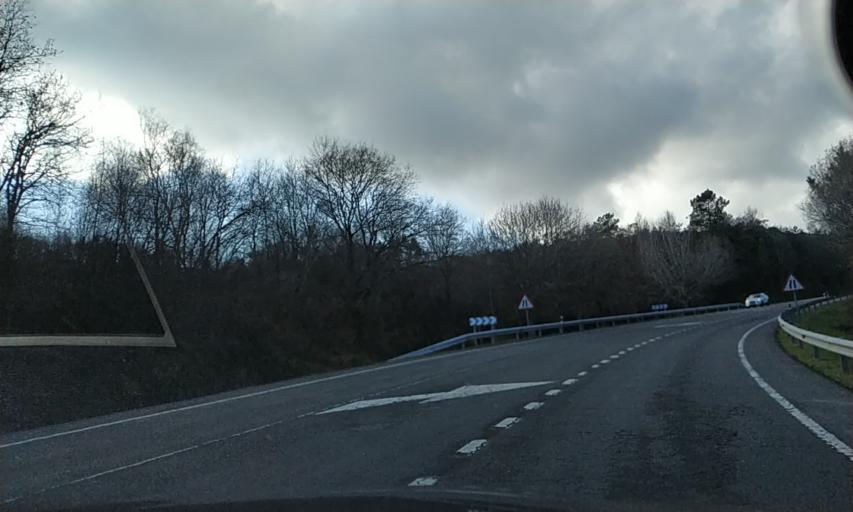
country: ES
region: Galicia
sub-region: Provincia de Pontevedra
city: Silleda
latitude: 42.6978
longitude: -8.3307
